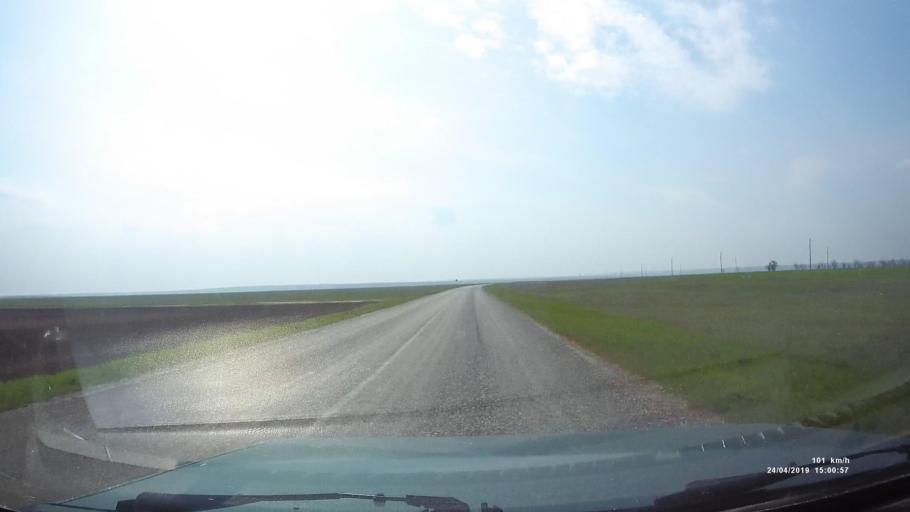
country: RU
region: Rostov
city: Remontnoye
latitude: 46.5654
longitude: 43.5443
